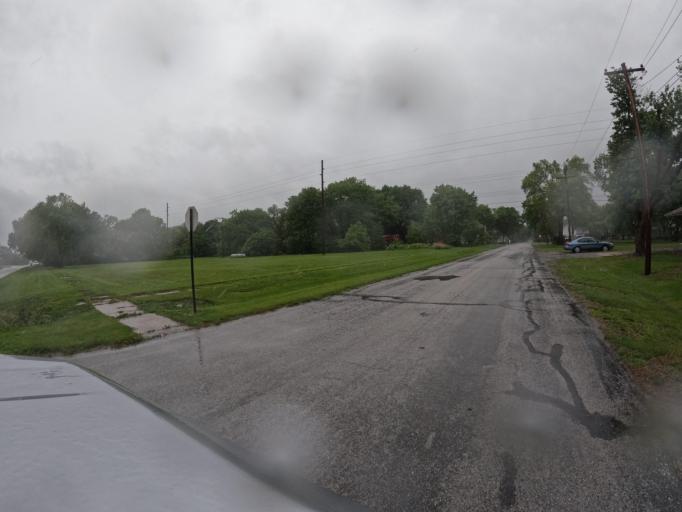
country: US
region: Nebraska
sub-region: Gage County
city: Wymore
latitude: 40.1377
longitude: -96.6637
